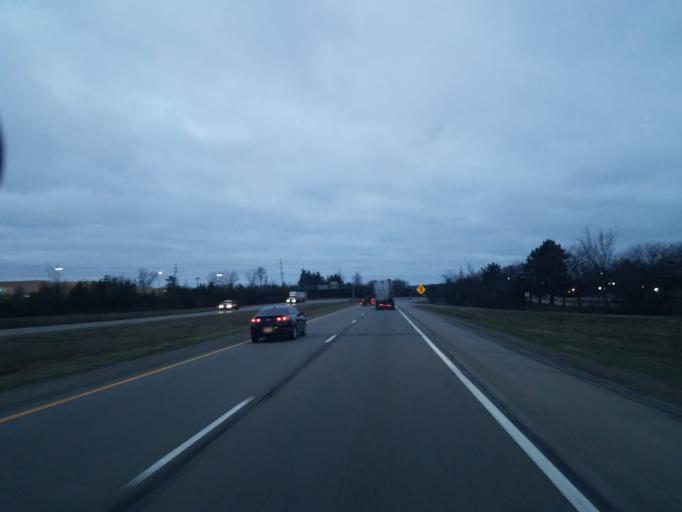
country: US
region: Michigan
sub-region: Washtenaw County
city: Ann Arbor
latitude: 42.2560
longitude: -83.6837
